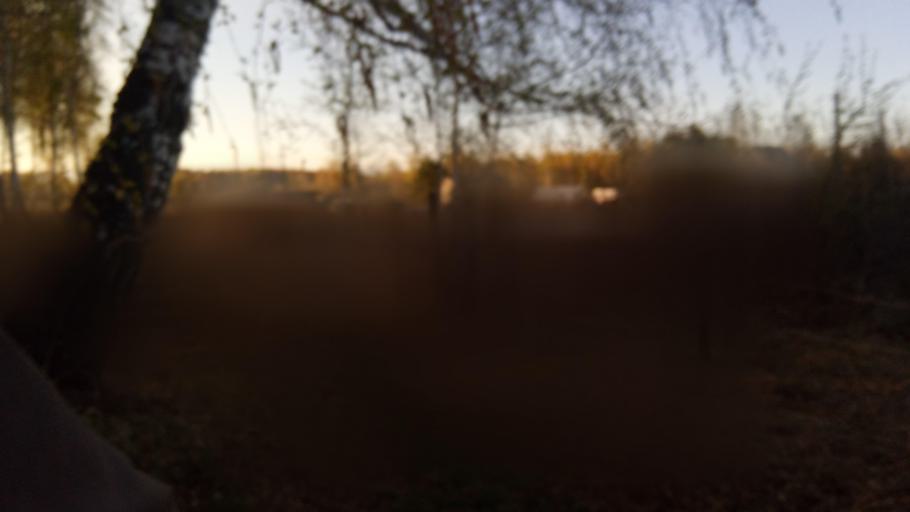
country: RU
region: Chelyabinsk
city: Timiryazevskiy
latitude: 54.9944
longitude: 60.8500
